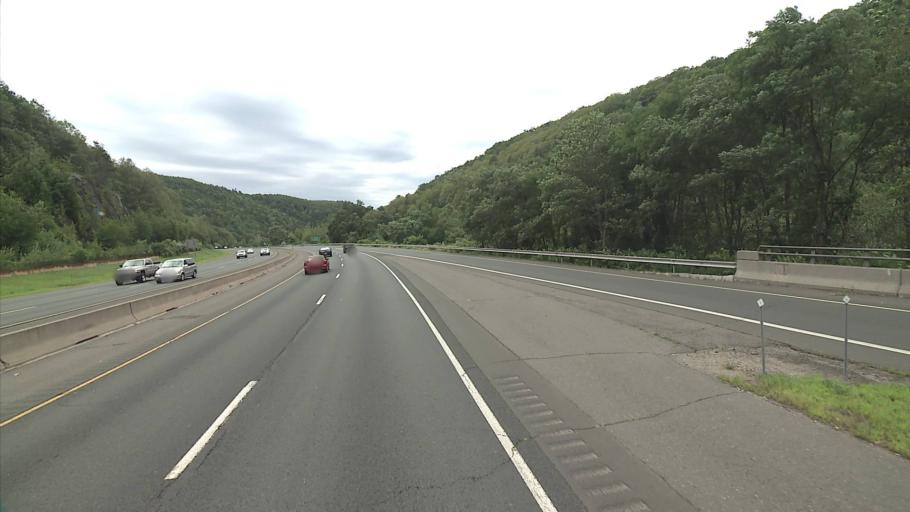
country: US
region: Connecticut
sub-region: New Haven County
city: Naugatuck
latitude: 41.4666
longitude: -73.0526
